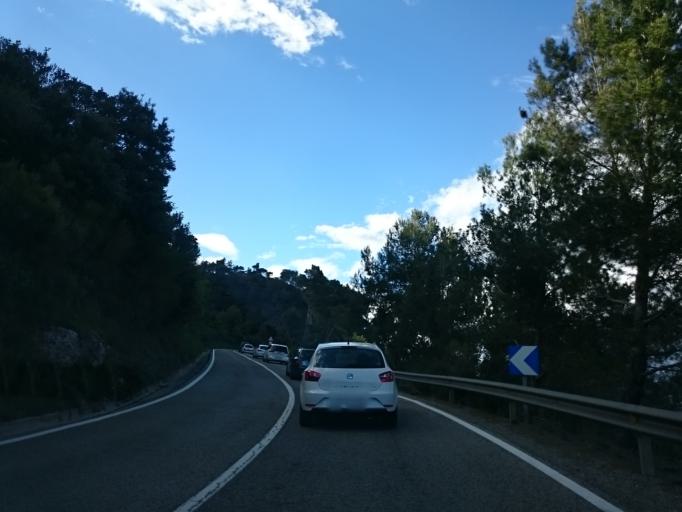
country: ES
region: Catalonia
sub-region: Provincia de Barcelona
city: Begues
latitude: 41.3246
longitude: 1.9504
